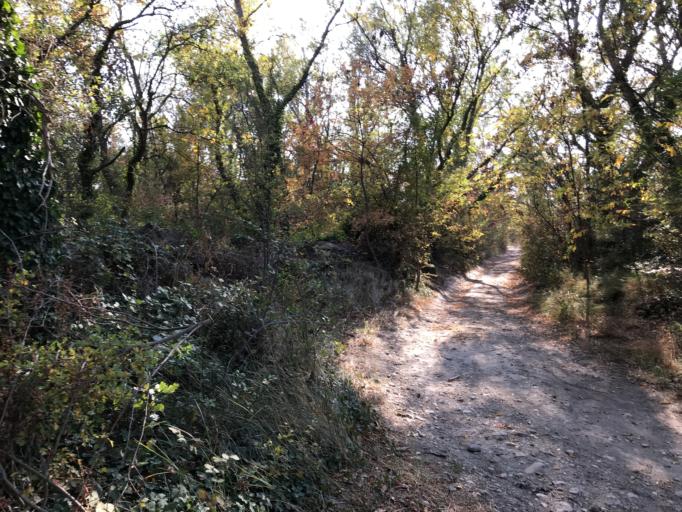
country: FR
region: Provence-Alpes-Cote d'Azur
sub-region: Departement des Bouches-du-Rhone
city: Mallemort
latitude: 43.7381
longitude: 5.1872
